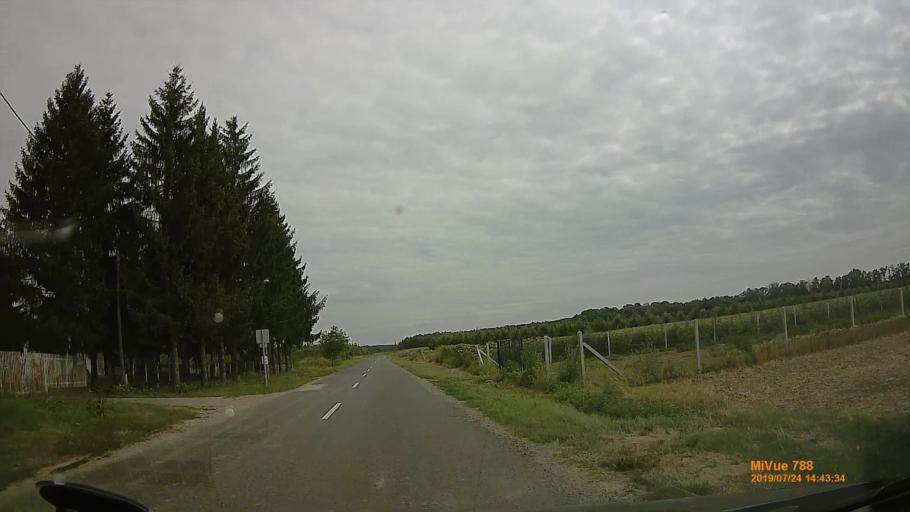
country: HU
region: Szabolcs-Szatmar-Bereg
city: Mandok
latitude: 48.3100
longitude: 22.2785
